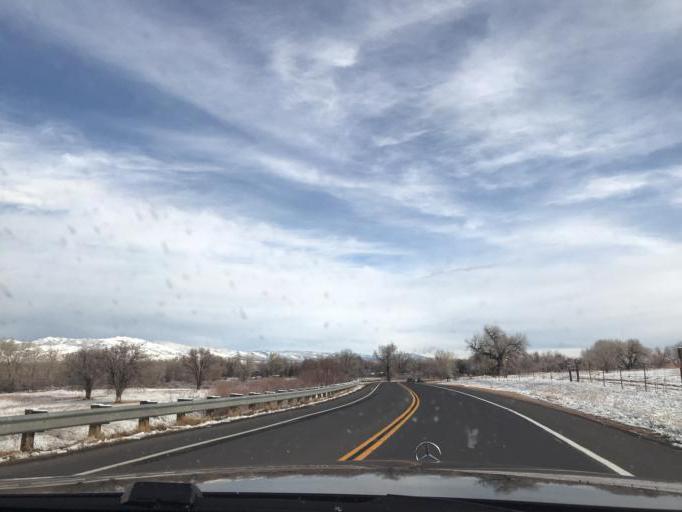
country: US
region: Colorado
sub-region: Boulder County
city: Superior
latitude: 39.9955
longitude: -105.2125
